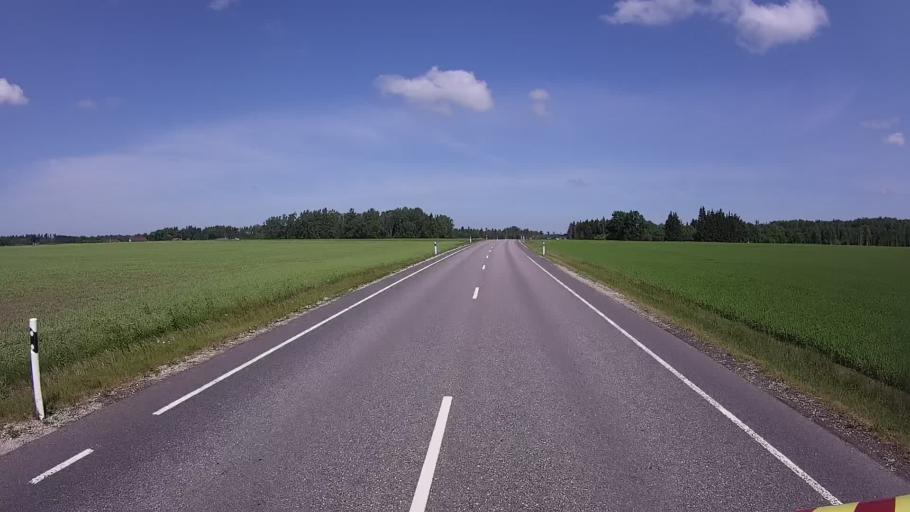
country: EE
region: Tartu
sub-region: Tartu linn
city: Tartu
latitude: 58.3737
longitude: 26.8838
